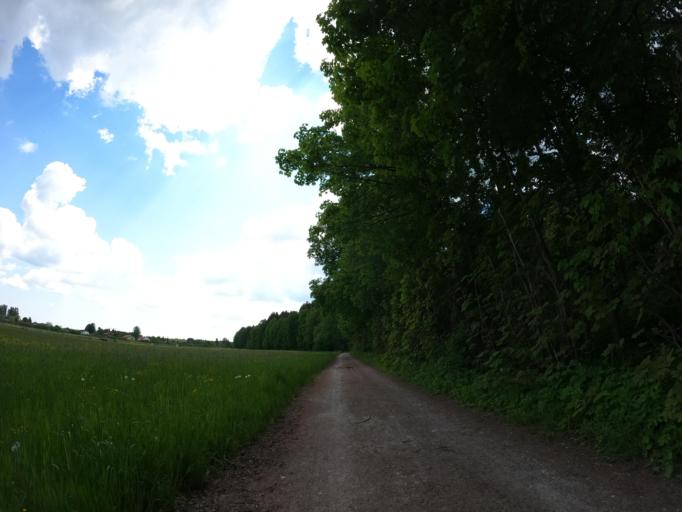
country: DE
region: Bavaria
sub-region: Upper Bavaria
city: Sauerlach
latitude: 47.9951
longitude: 11.6371
